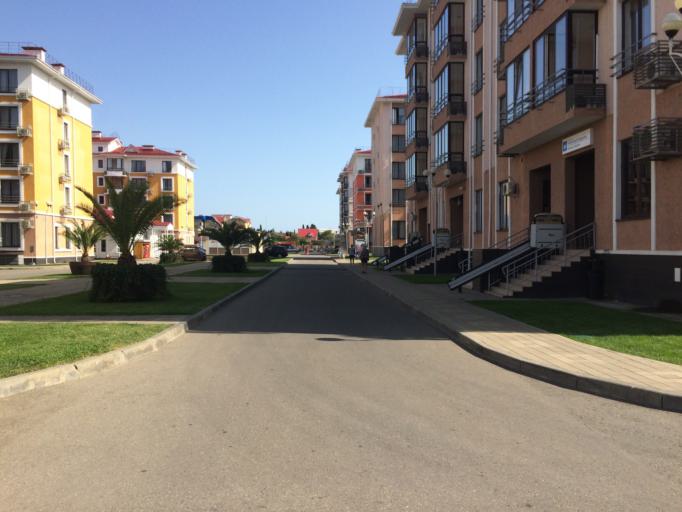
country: RU
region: Krasnodarskiy
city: Adler
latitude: 43.3965
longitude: 39.9773
